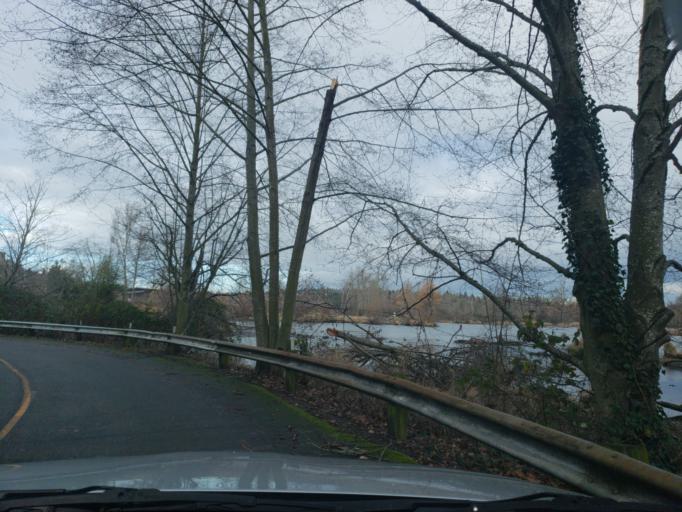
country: US
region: Washington
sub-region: King County
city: Seattle
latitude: 47.6520
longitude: -122.2986
